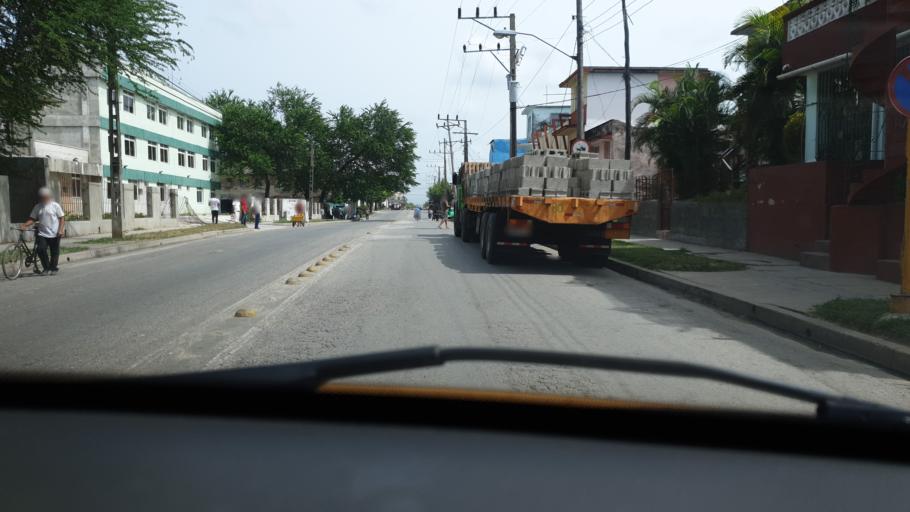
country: CU
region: Villa Clara
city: Santa Clara
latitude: 22.3938
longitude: -79.9616
